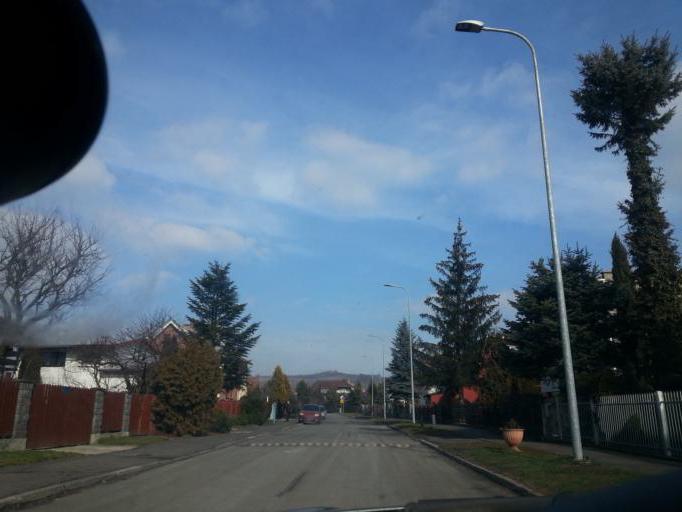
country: PL
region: Lower Silesian Voivodeship
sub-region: Powiat jeleniogorski
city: Jezow Sudecki
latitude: 50.9167
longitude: 15.7460
